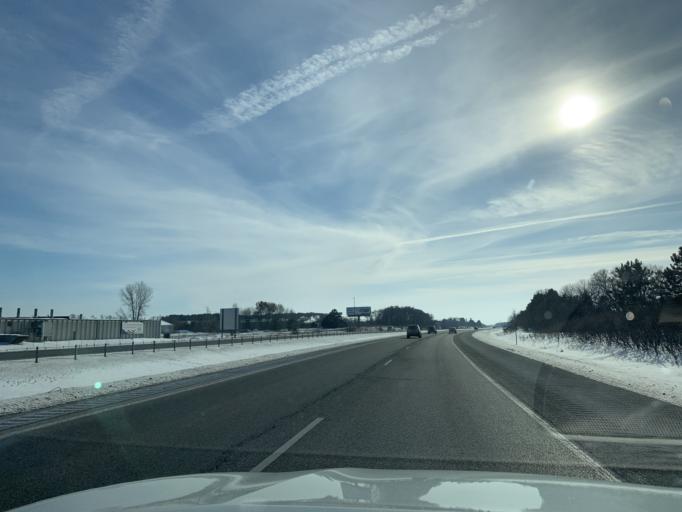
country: US
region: Minnesota
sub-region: Chisago County
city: Wyoming
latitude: 45.3258
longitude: -93.0038
